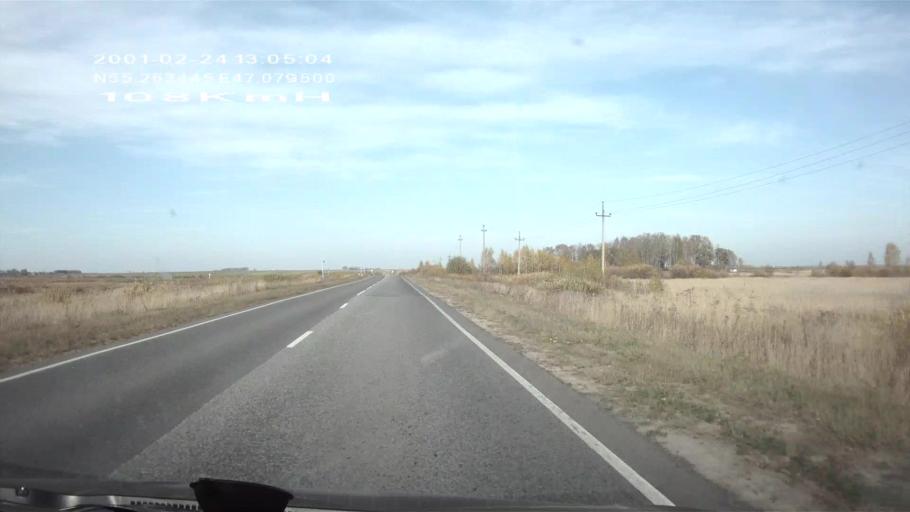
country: RU
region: Chuvashia
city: Ibresi
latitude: 55.2636
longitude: 47.0795
